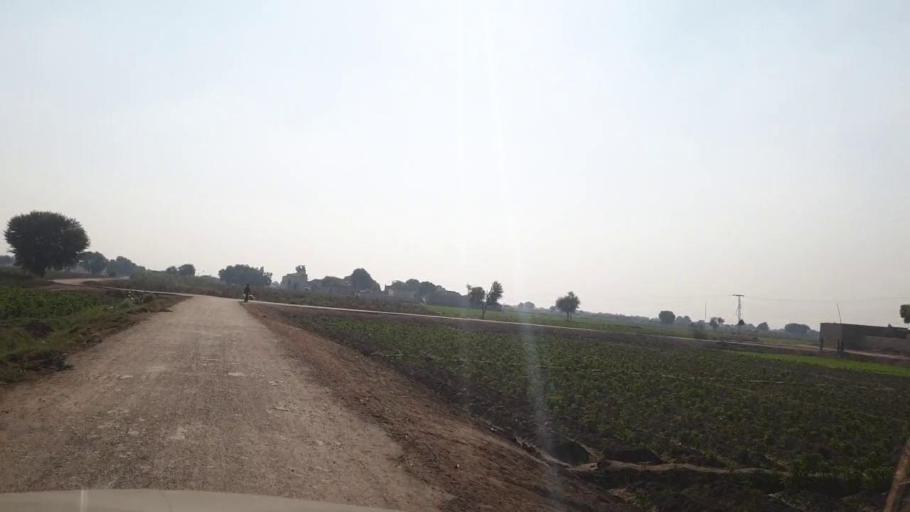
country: PK
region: Sindh
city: Bhan
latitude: 26.5318
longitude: 67.7435
